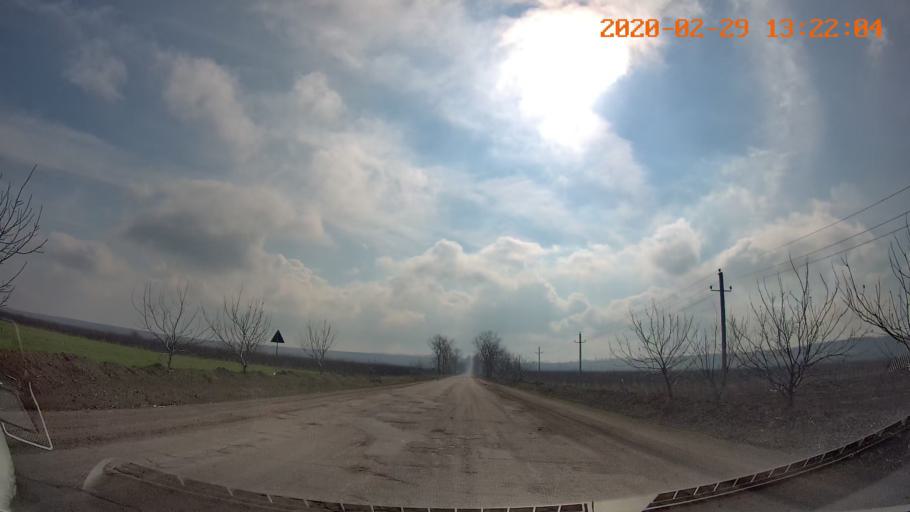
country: MD
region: Telenesti
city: Camenca
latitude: 47.9644
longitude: 28.6286
